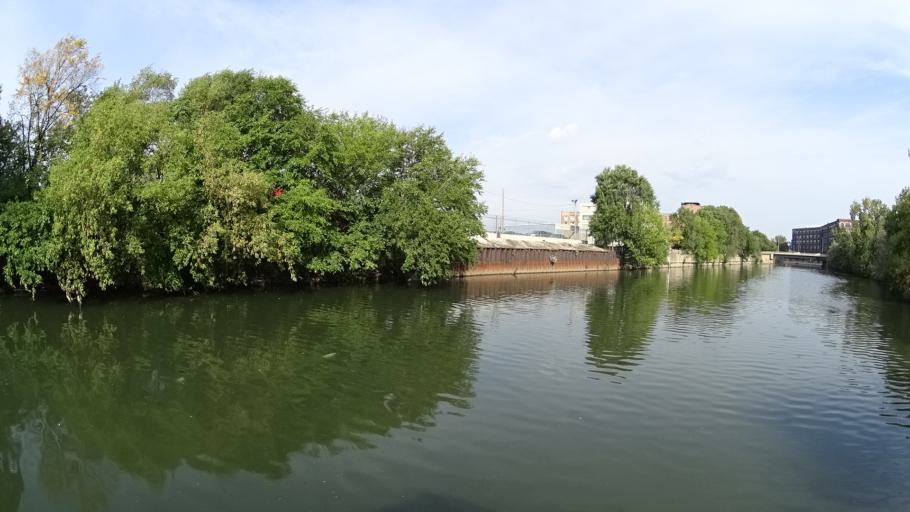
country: US
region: Illinois
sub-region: Cook County
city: Chicago
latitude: 41.8283
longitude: -87.6576
